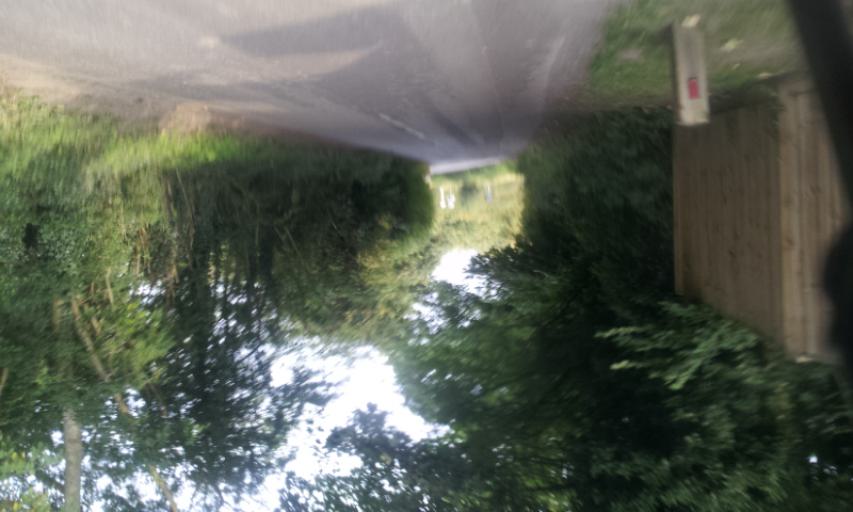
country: GB
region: England
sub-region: Kent
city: Wateringbury
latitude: 51.2405
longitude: 0.4227
